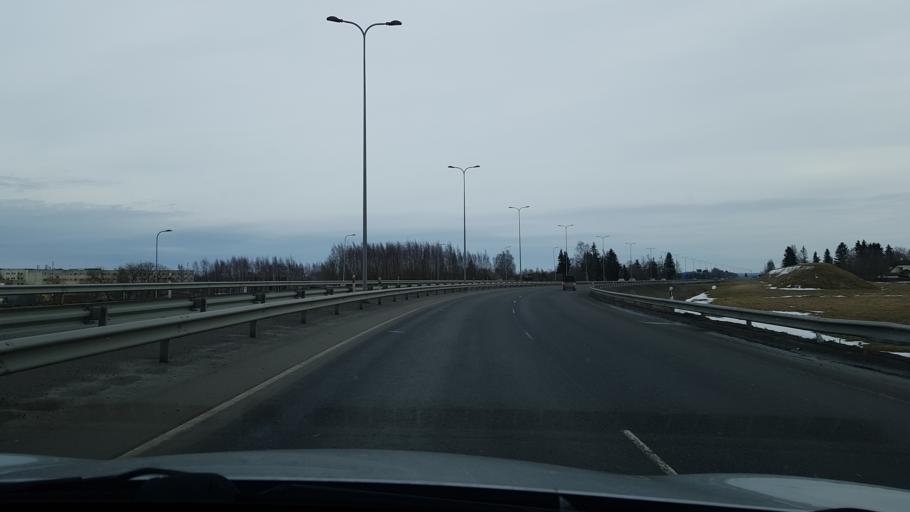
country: EE
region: Tartu
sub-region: UElenurme vald
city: Ulenurme
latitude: 58.3434
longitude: 26.7112
